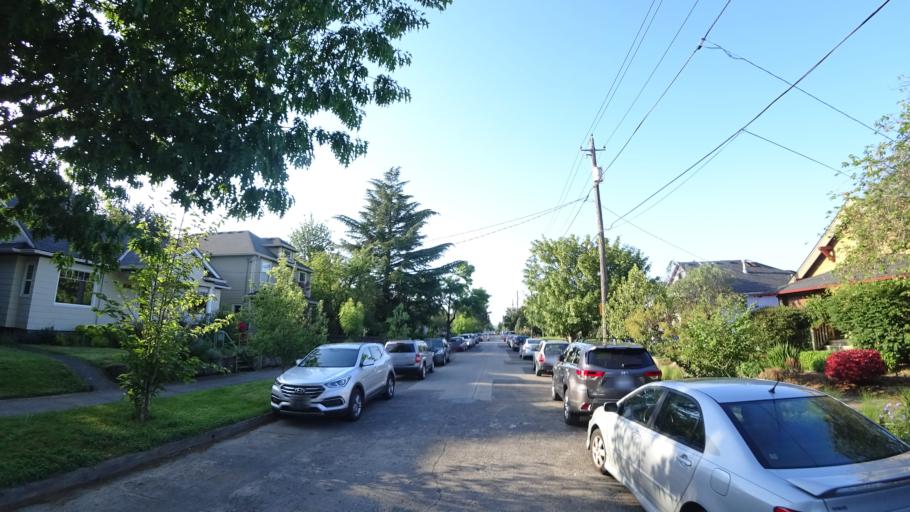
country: US
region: Oregon
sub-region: Multnomah County
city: Portland
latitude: 45.5578
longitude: -122.6338
